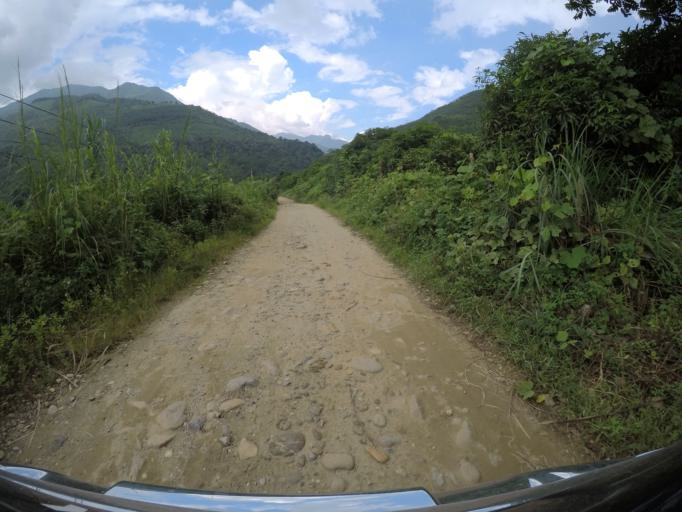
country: VN
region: Yen Bai
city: Son Thinh
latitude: 21.6649
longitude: 104.5120
